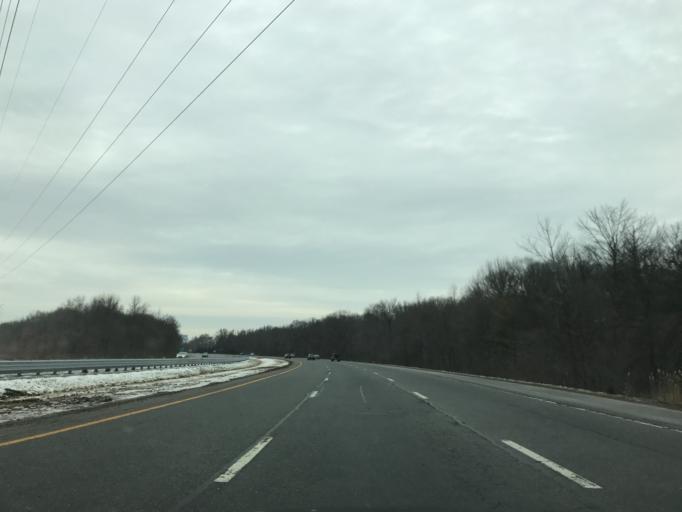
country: US
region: New Jersey
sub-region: Mercer County
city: Mercerville
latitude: 40.2205
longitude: -74.6979
